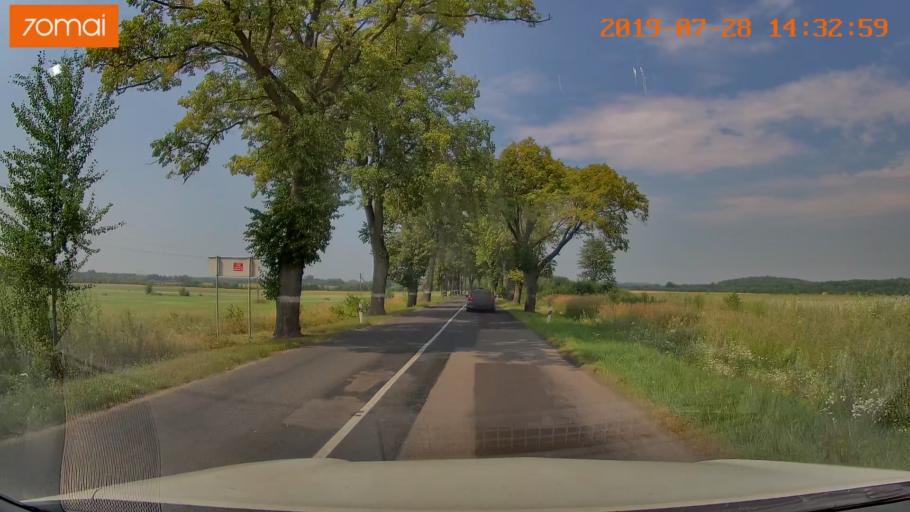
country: RU
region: Kaliningrad
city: Primorsk
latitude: 54.8163
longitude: 20.0362
